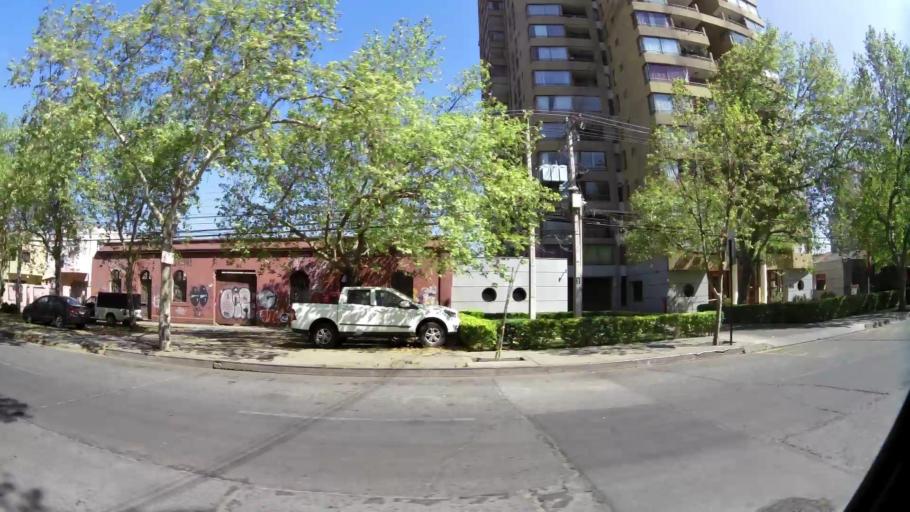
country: CL
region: Santiago Metropolitan
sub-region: Provincia de Santiago
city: Santiago
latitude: -33.4641
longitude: -70.6637
